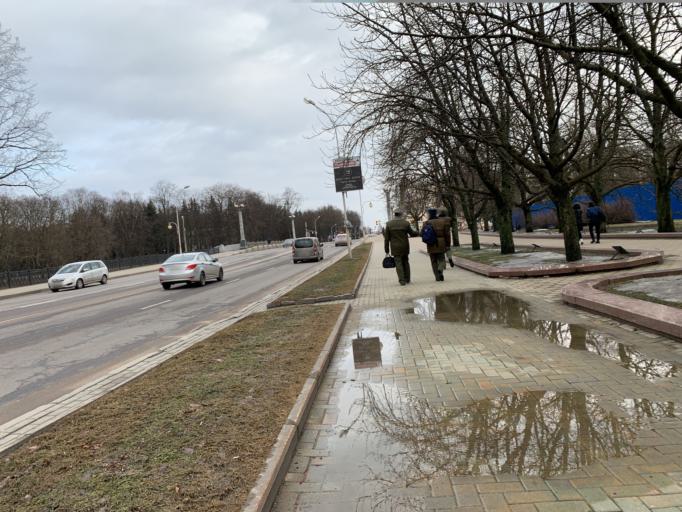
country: BY
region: Minsk
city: Minsk
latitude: 53.9073
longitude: 27.5623
